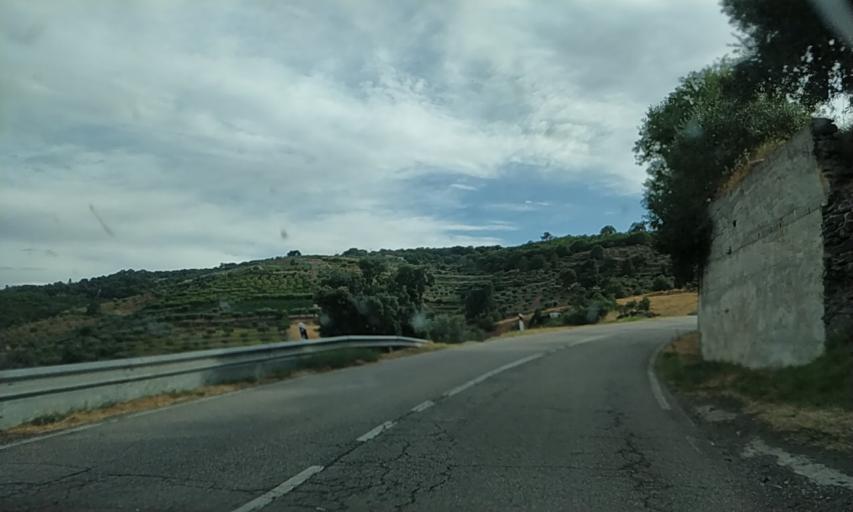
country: PT
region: Viseu
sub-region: Penedono
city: Penedono
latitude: 41.0671
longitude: -7.3976
